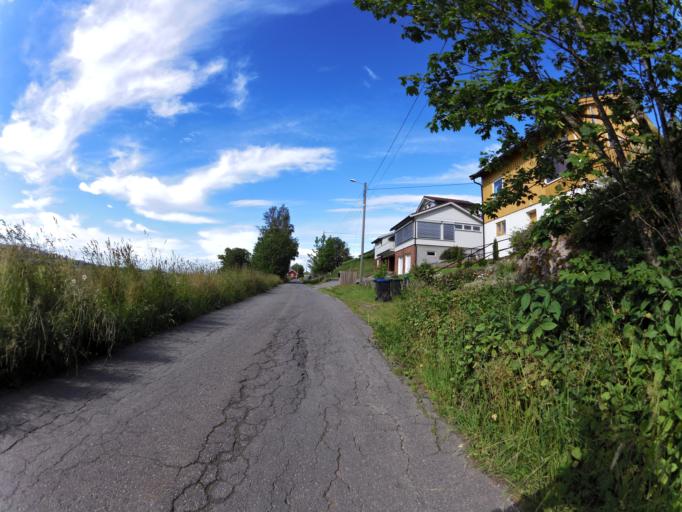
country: NO
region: Ostfold
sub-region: Fredrikstad
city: Fredrikstad
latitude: 59.2490
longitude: 11.0070
